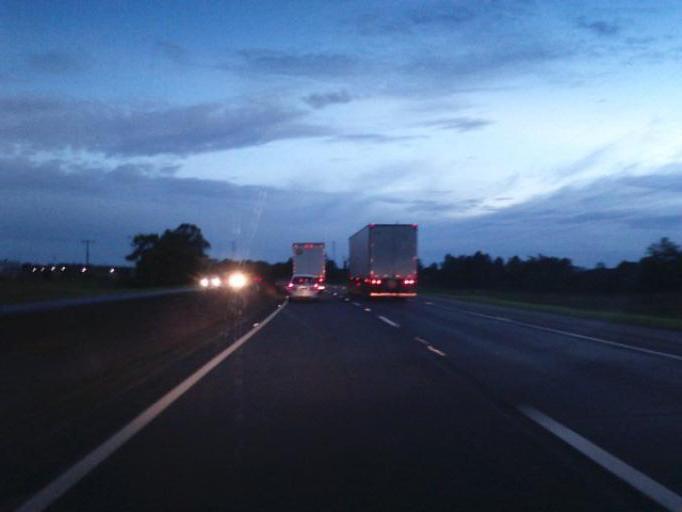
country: BR
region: Santa Catarina
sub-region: Barra Velha
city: Barra Velha
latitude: -26.4933
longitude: -48.7335
